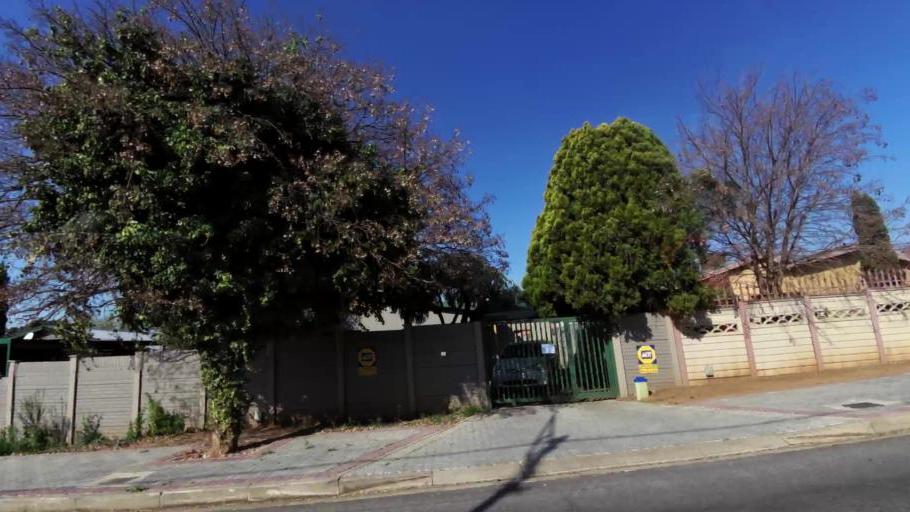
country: ZA
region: Gauteng
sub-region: City of Johannesburg Metropolitan Municipality
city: Johannesburg
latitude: -26.1751
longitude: 27.9842
